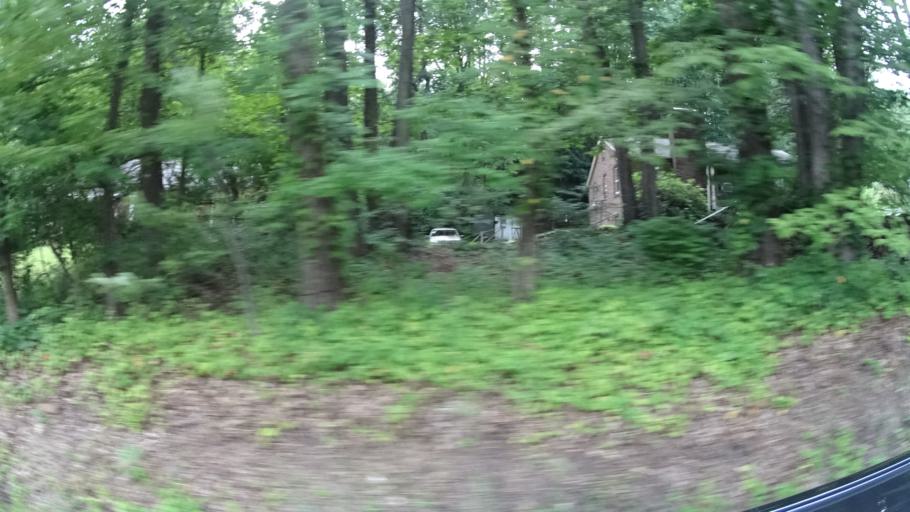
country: US
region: New Jersey
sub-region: Somerset County
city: Warren Township
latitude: 40.6229
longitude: -74.4973
